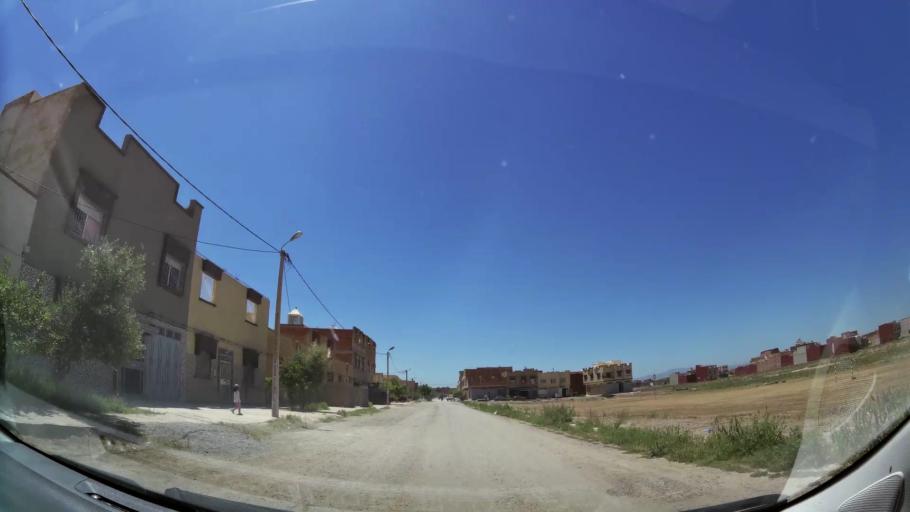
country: MA
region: Oriental
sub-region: Oujda-Angad
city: Oujda
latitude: 34.6781
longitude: -1.8548
